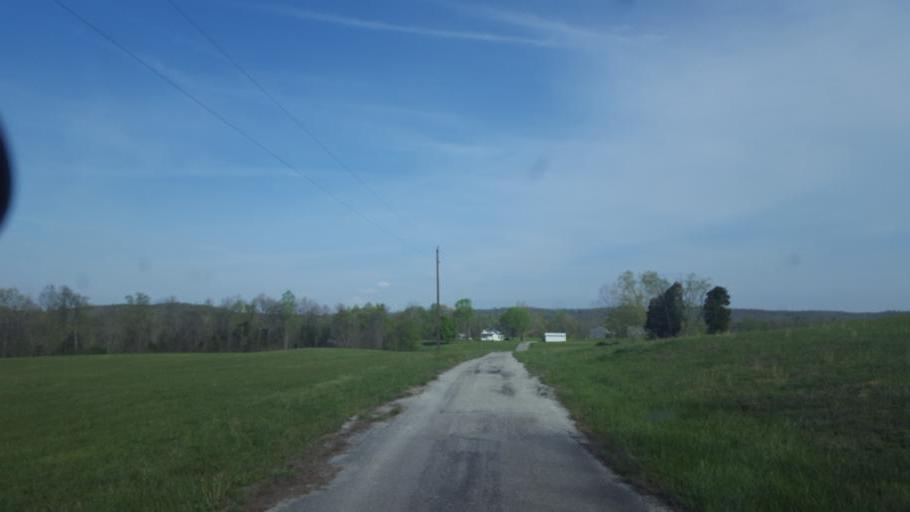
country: US
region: Kentucky
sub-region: Edmonson County
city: Brownsville
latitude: 37.3315
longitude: -86.1121
